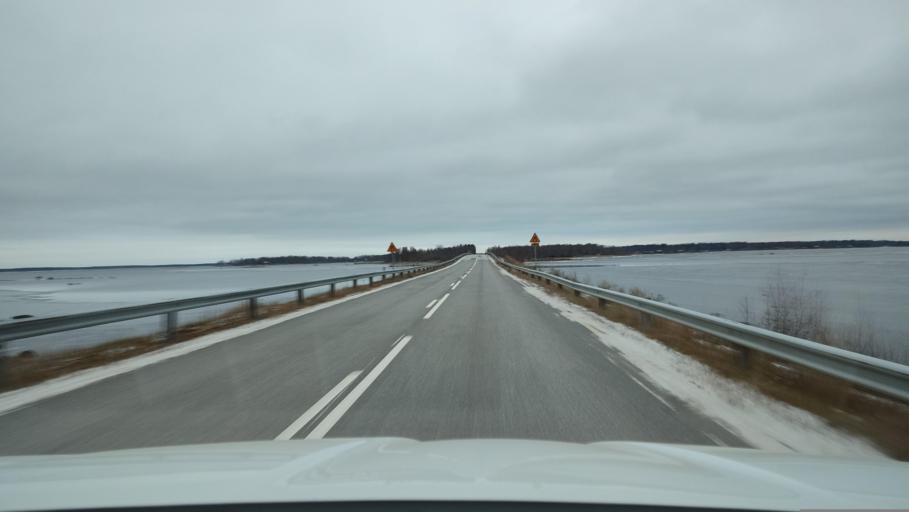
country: FI
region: Ostrobothnia
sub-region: Vaasa
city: Replot
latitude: 63.2718
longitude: 21.3451
